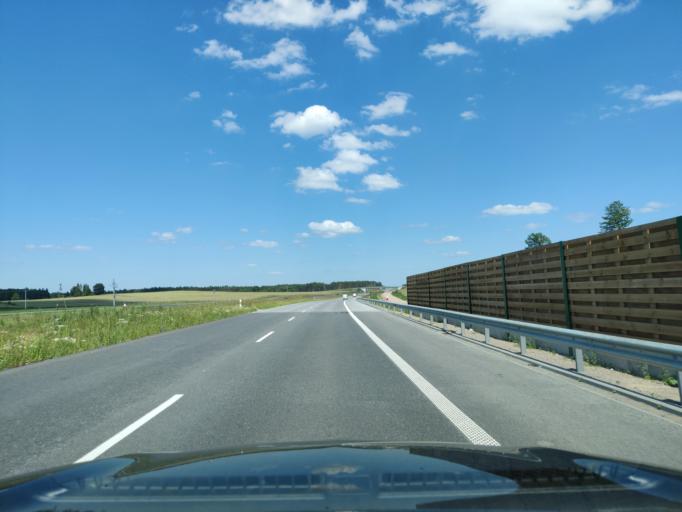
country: PL
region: Masovian Voivodeship
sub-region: Powiat mlawski
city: Strzegowo
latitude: 52.9687
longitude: 20.3191
